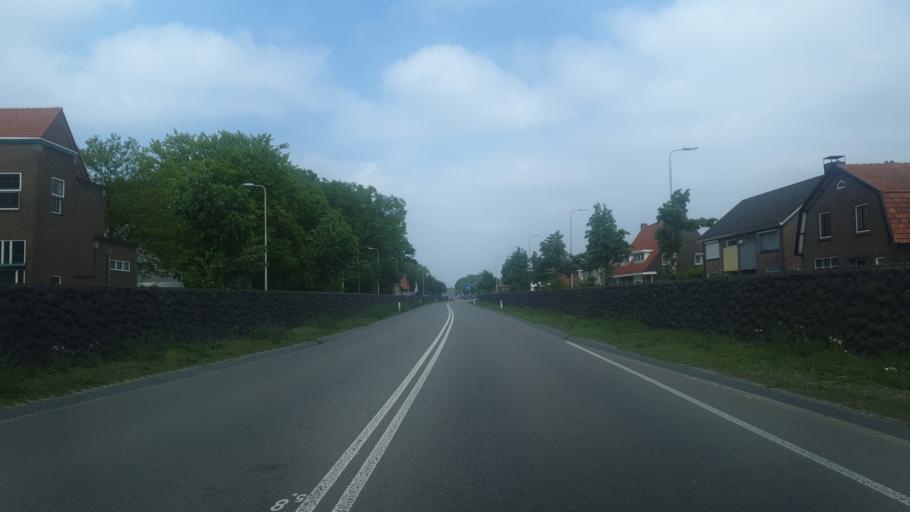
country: NL
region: Gelderland
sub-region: Gemeente Wijchen
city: Wijchen
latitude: 51.8045
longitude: 5.7565
